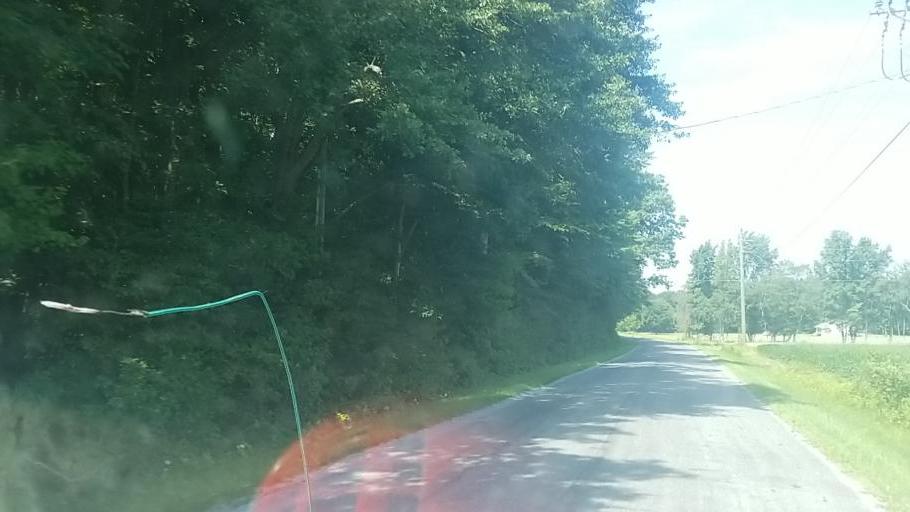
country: US
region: Maryland
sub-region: Caroline County
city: Denton
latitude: 38.8785
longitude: -75.7737
